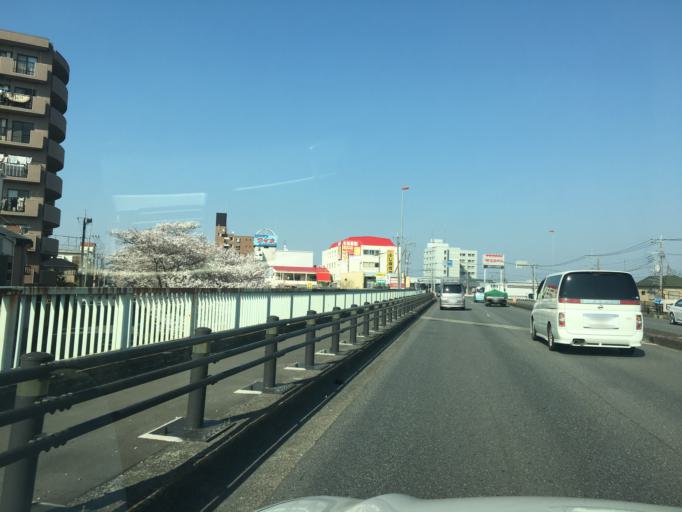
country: JP
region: Saitama
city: Kawagoe
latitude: 35.9091
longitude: 139.4961
